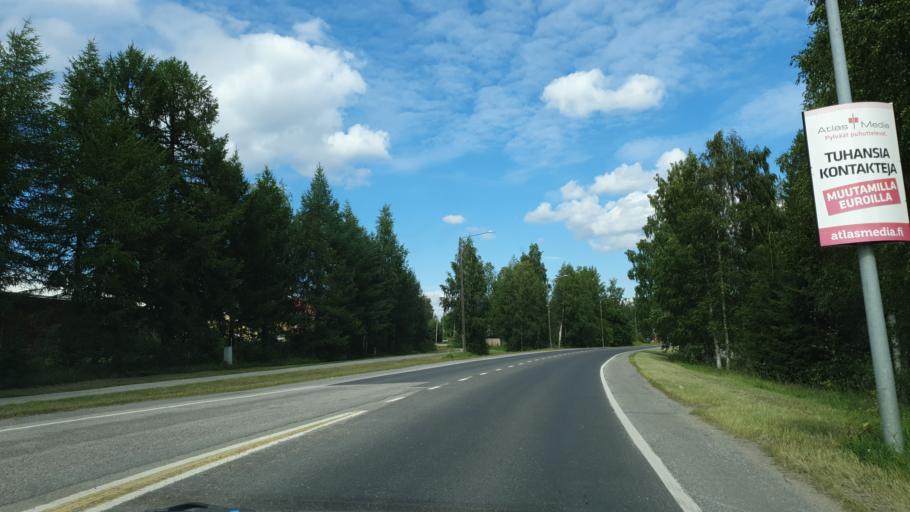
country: FI
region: Kainuu
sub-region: Kajaani
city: Kajaani
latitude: 64.2385
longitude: 27.7498
